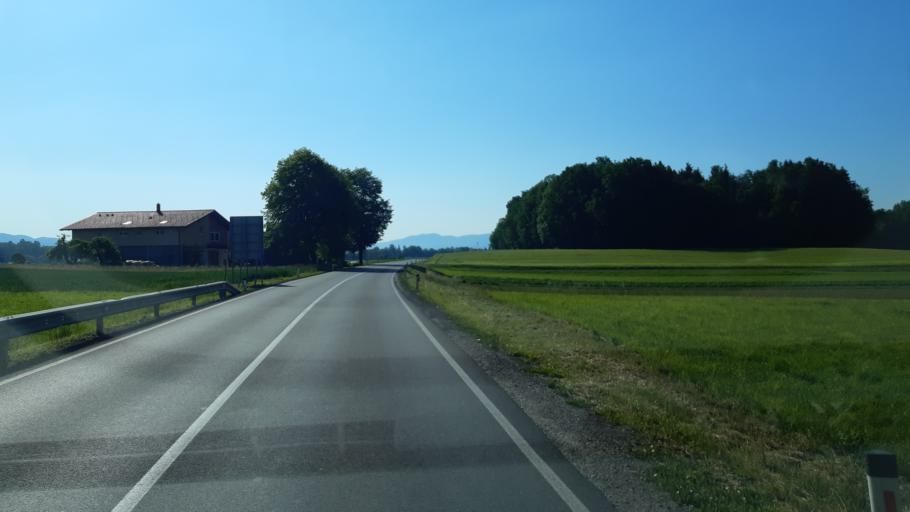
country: SI
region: Komenda
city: Komenda
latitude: 46.2014
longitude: 14.5336
